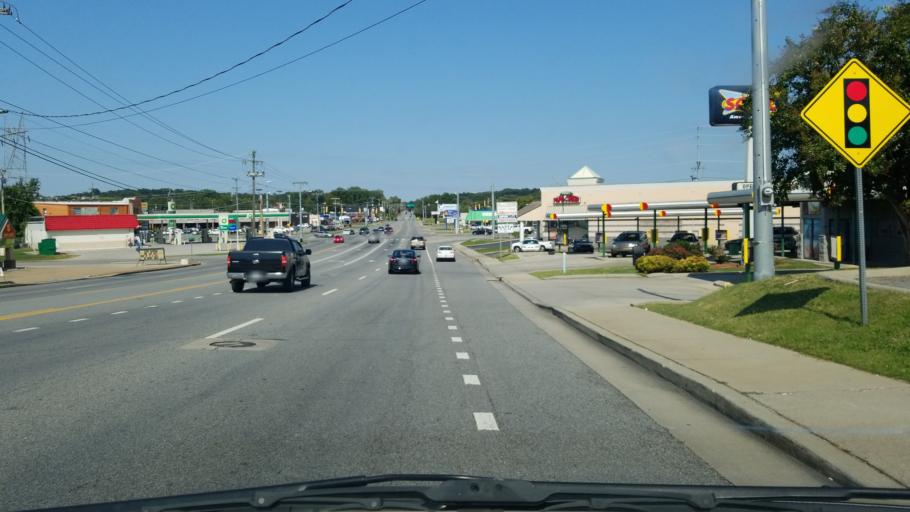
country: US
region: Tennessee
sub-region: Hamilton County
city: East Brainerd
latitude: 35.0444
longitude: -85.1608
